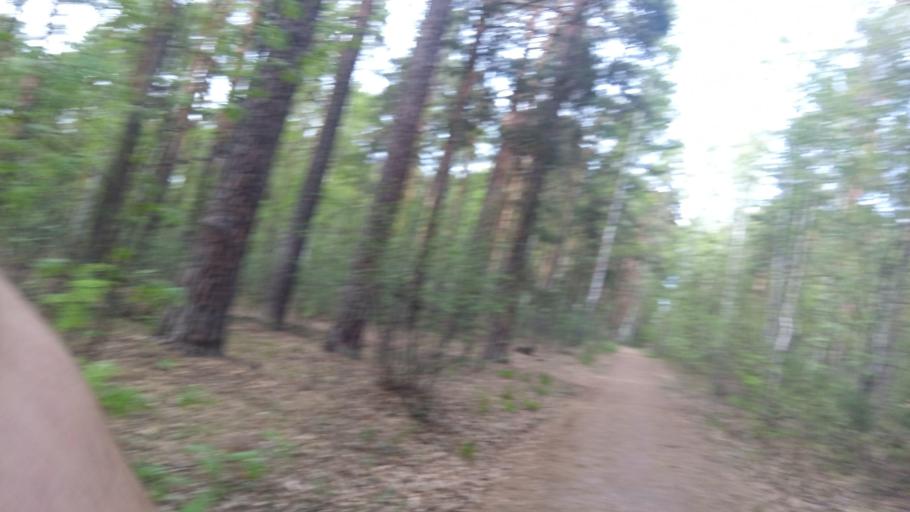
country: RU
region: Chelyabinsk
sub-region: Gorod Chelyabinsk
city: Chelyabinsk
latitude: 55.1568
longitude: 61.3432
